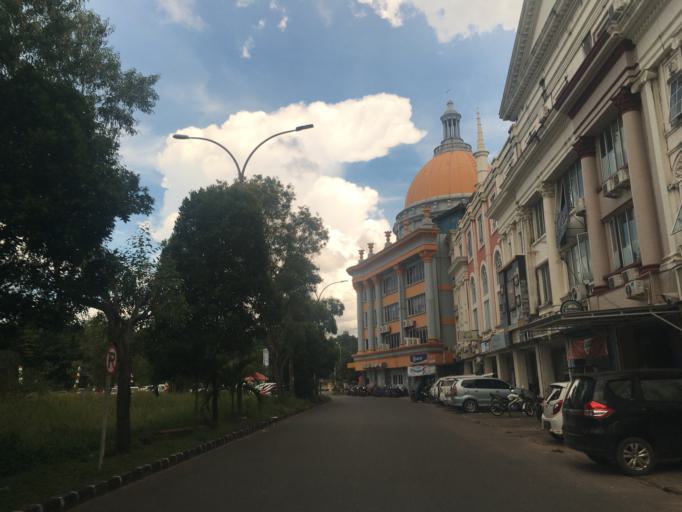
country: SG
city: Singapore
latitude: 1.1175
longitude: 104.0239
